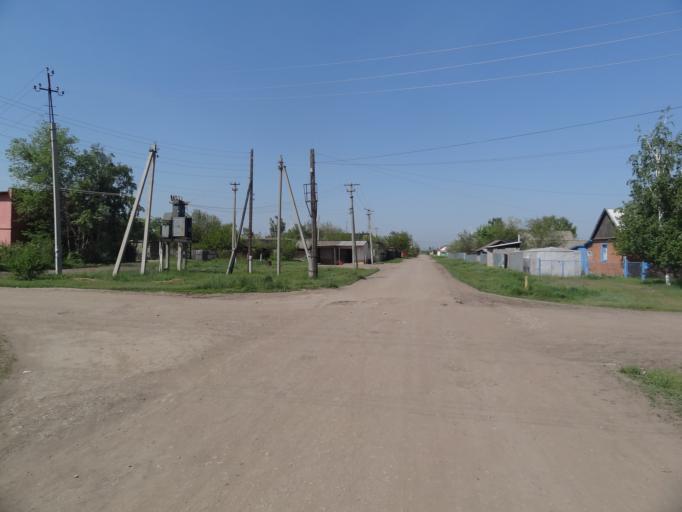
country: RU
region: Saratov
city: Privolzhskiy
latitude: 51.4138
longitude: 46.0975
